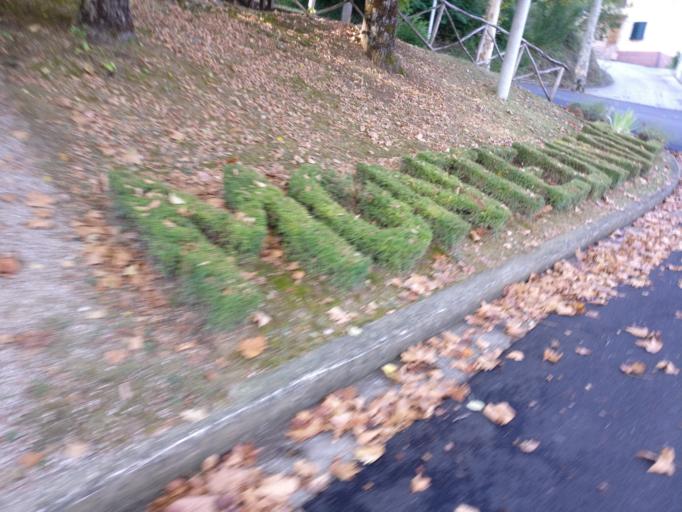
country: IT
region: The Marches
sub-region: Provincia di Ascoli Piceno
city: Montedinove
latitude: 42.9731
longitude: 13.5898
